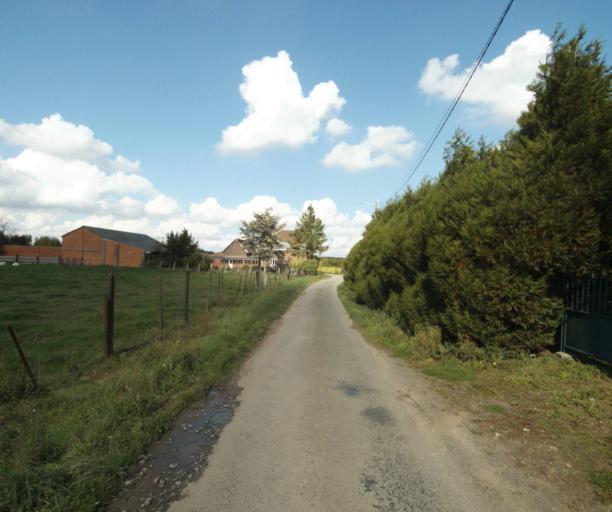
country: FR
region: Nord-Pas-de-Calais
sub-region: Departement du Pas-de-Calais
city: Lorgies
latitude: 50.5720
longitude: 2.8084
